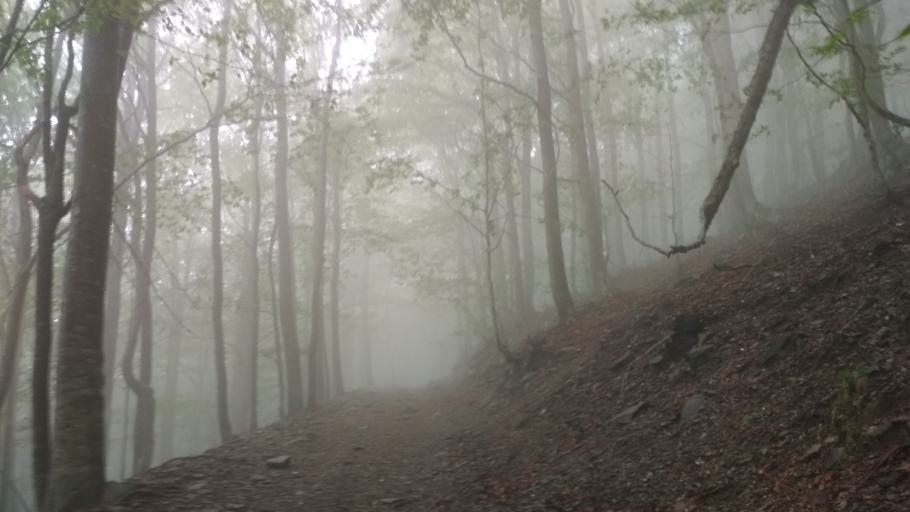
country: ES
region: Catalonia
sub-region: Provincia de Barcelona
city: Fogars de Montclus
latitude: 41.7750
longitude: 2.4476
